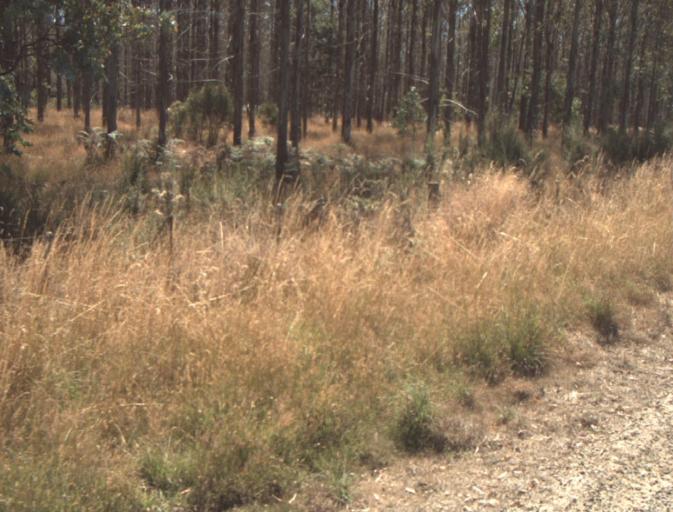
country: AU
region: Tasmania
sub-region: Dorset
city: Scottsdale
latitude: -41.3260
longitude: 147.4446
